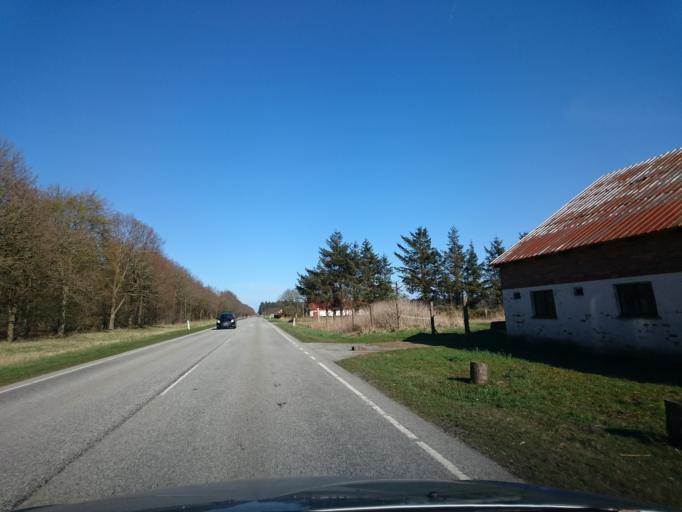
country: DK
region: North Denmark
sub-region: Hjorring Kommune
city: Sindal
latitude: 57.5872
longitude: 10.2408
